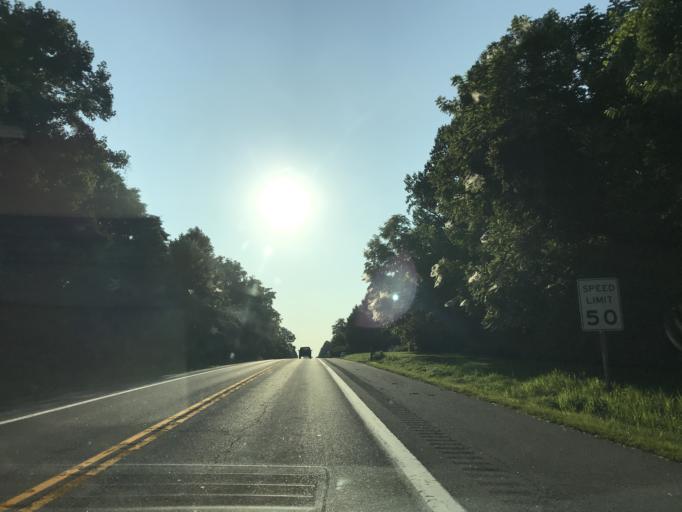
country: US
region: Maryland
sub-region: Cecil County
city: Elkton
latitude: 39.6990
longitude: -75.8428
